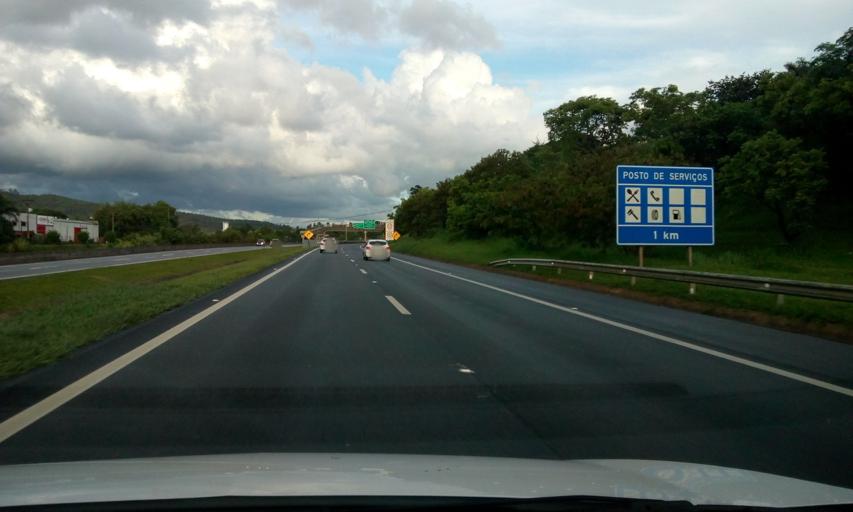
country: BR
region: Sao Paulo
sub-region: Atibaia
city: Atibaia
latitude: -23.1076
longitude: -46.5106
